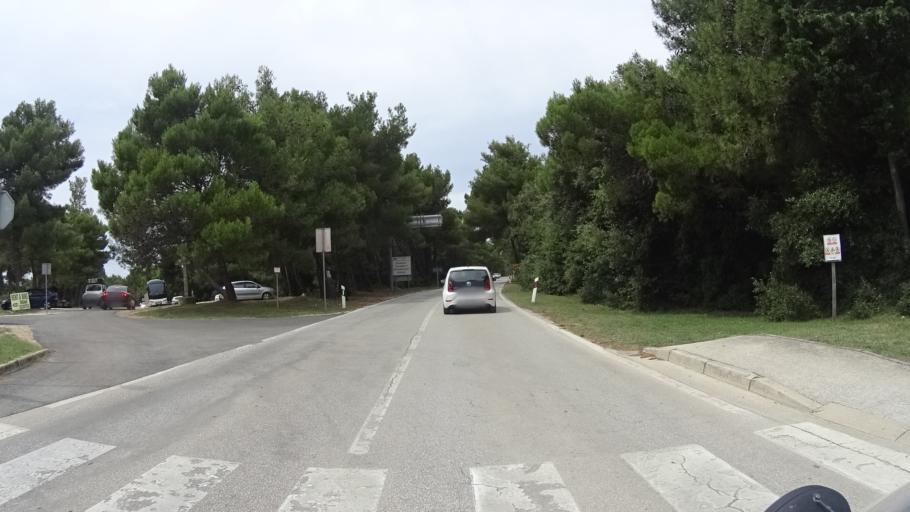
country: HR
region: Istarska
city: Medulin
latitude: 44.8059
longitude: 13.9092
